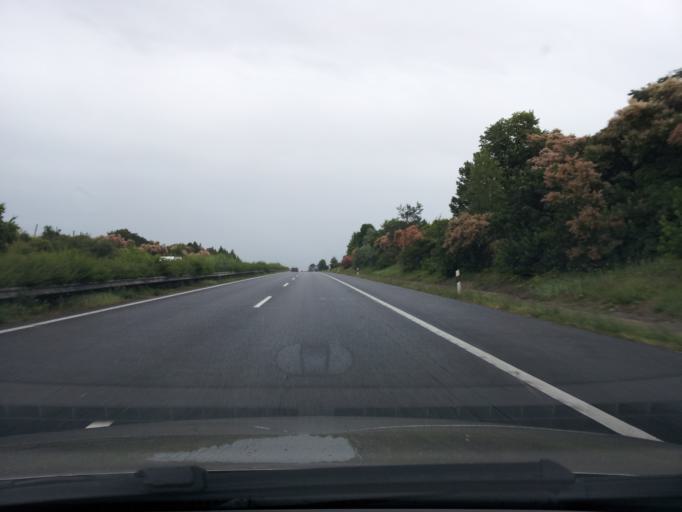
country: HU
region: Fejer
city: Lepseny
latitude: 47.0169
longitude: 18.2481
